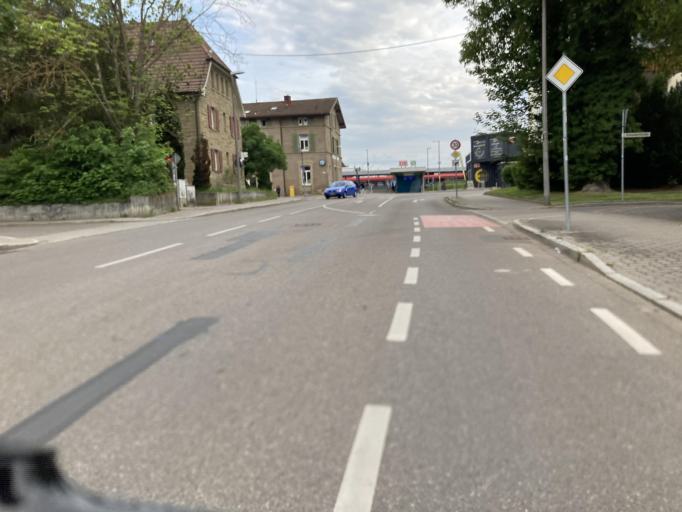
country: DE
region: Baden-Wuerttemberg
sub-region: Regierungsbezirk Stuttgart
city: Renningen
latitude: 48.7743
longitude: 8.9330
